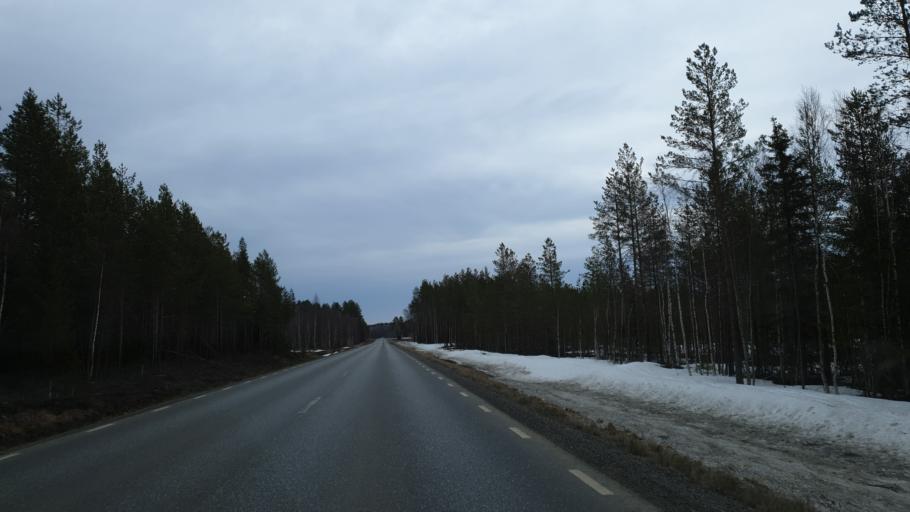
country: SE
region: Vaesterbotten
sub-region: Robertsfors Kommun
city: Robertsfors
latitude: 64.2324
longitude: 20.9832
